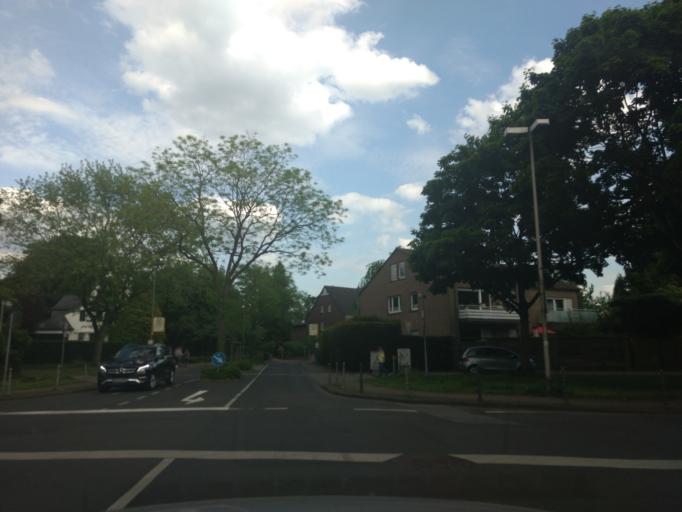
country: DE
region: North Rhine-Westphalia
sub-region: Regierungsbezirk Dusseldorf
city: Meerbusch
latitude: 51.2510
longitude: 6.6983
